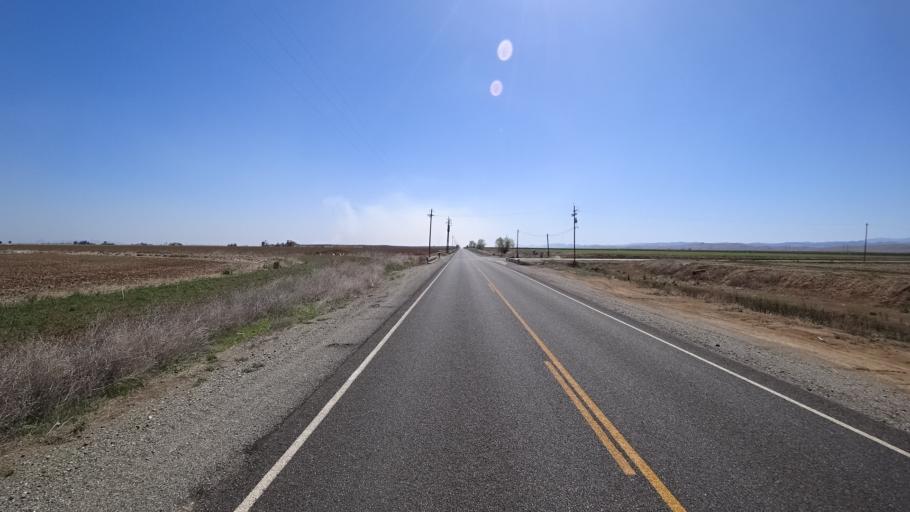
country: US
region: California
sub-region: Glenn County
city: Willows
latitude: 39.4663
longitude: -122.2489
